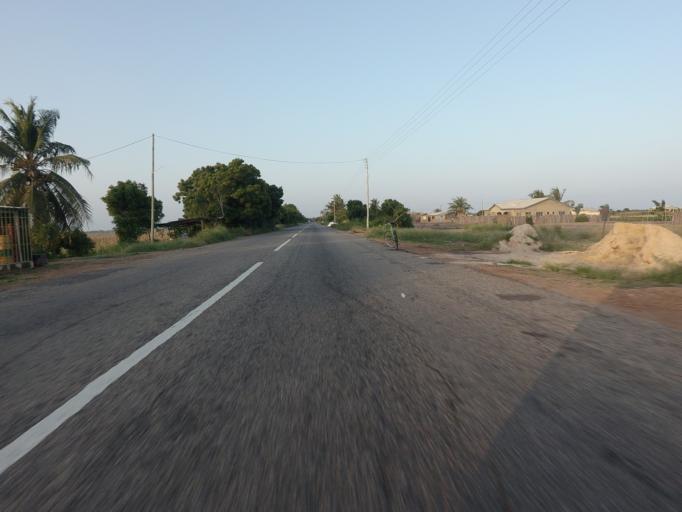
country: GH
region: Volta
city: Anloga
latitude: 5.7849
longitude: 0.8514
